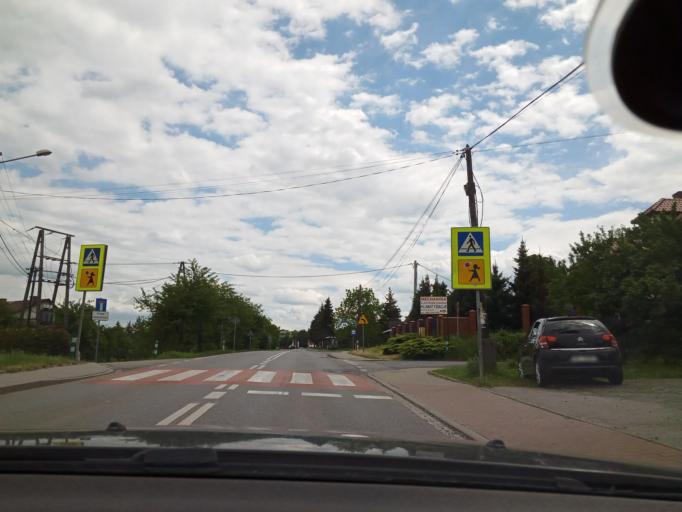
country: PL
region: Lesser Poland Voivodeship
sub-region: Powiat wielicki
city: Trabki
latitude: 49.9586
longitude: 20.1459
